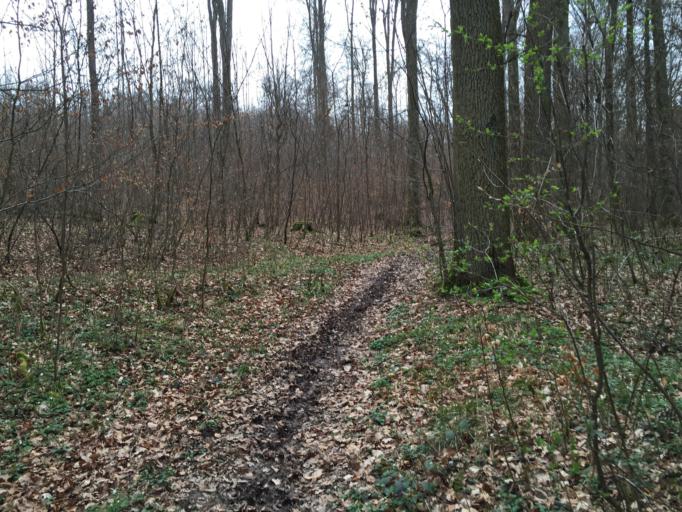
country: DE
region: Baden-Wuerttemberg
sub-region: Regierungsbezirk Stuttgart
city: Wernau
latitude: 48.6967
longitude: 9.4357
